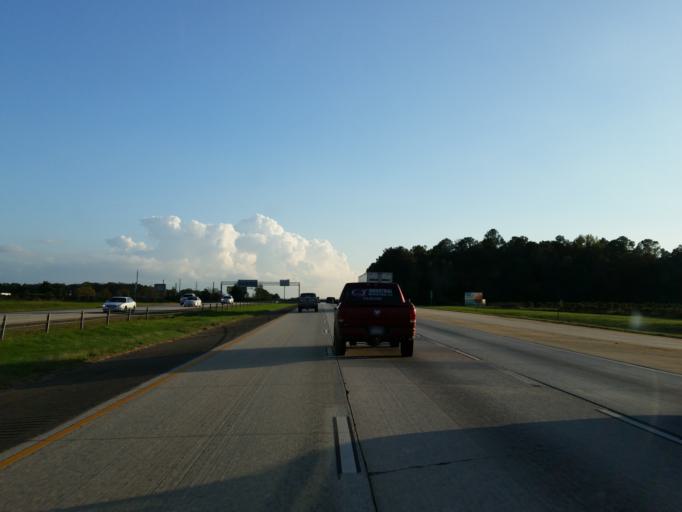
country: US
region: Georgia
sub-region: Houston County
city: Centerville
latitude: 32.5827
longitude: -83.7434
